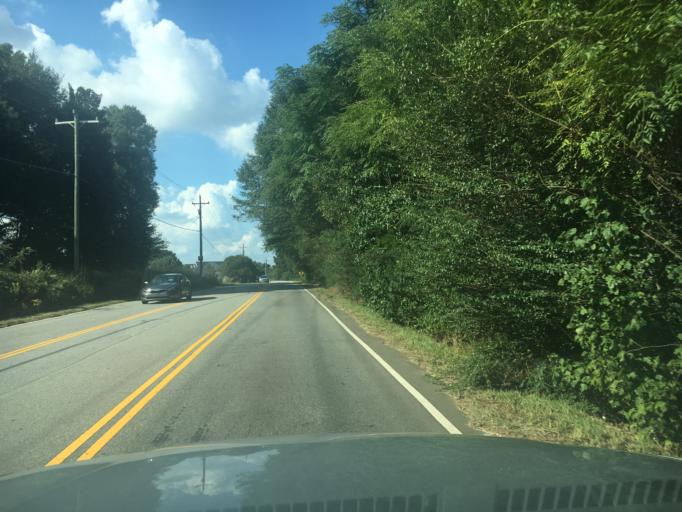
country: US
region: South Carolina
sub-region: Greenville County
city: Simpsonville
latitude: 34.6912
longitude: -82.2527
